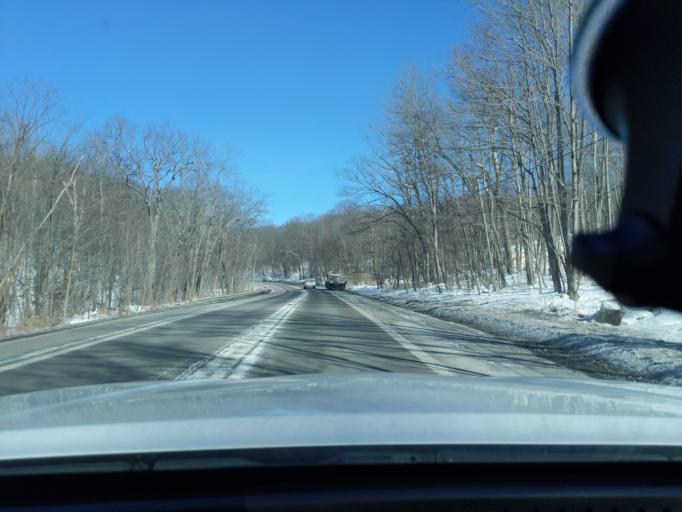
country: US
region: Maryland
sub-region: Allegany County
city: Frostburg
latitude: 39.6019
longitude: -78.9222
